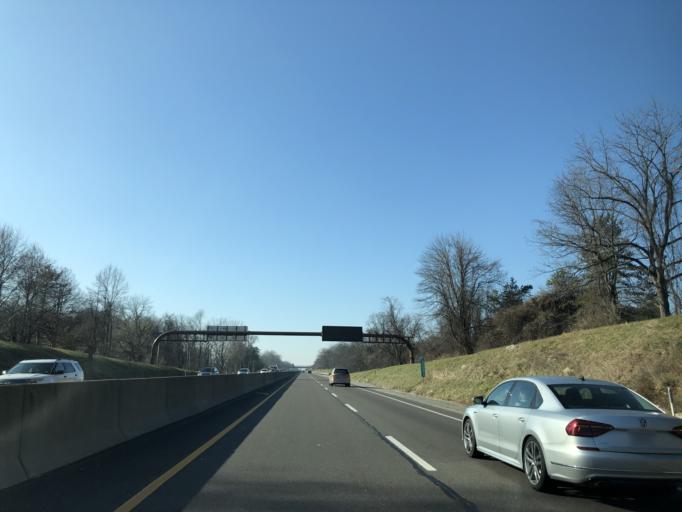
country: US
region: Pennsylvania
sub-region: Chester County
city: Chesterbrook
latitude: 40.0786
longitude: -75.4667
